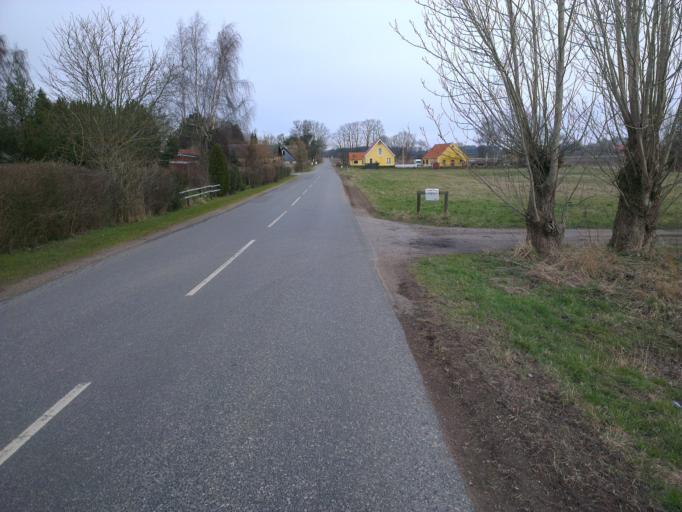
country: DK
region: Capital Region
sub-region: Frederikssund Kommune
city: Jaegerspris
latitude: 55.8104
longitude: 11.9514
